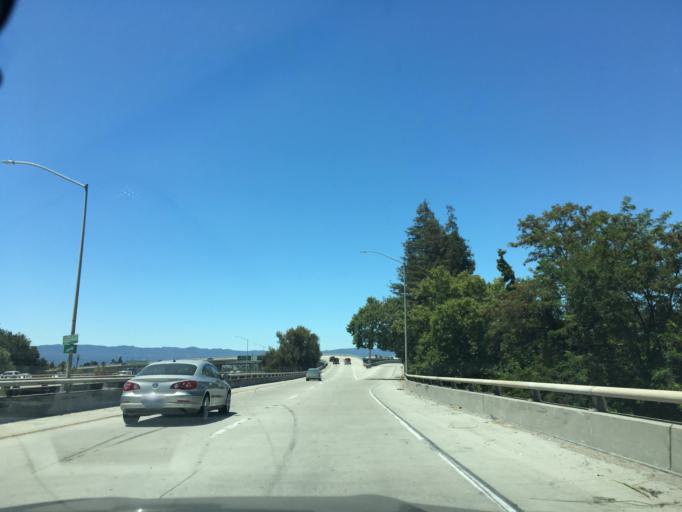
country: US
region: California
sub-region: Santa Clara County
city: San Jose
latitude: 37.3250
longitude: -121.8880
